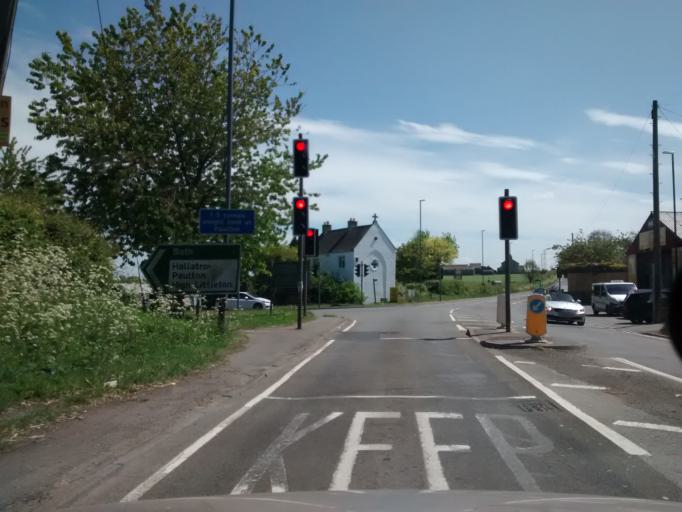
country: GB
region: England
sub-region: Bath and North East Somerset
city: Clutton
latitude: 51.3101
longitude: -2.5336
